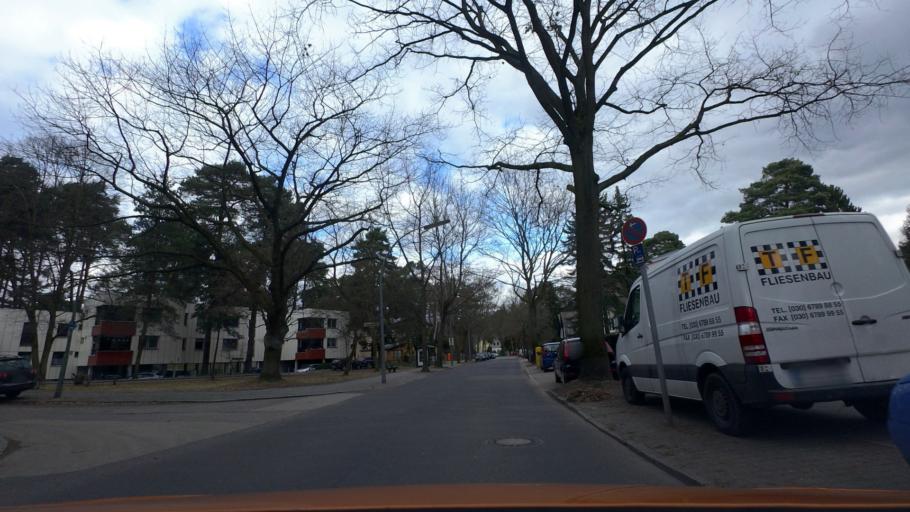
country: DE
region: Berlin
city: Konradshohe
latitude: 52.5902
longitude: 13.2244
